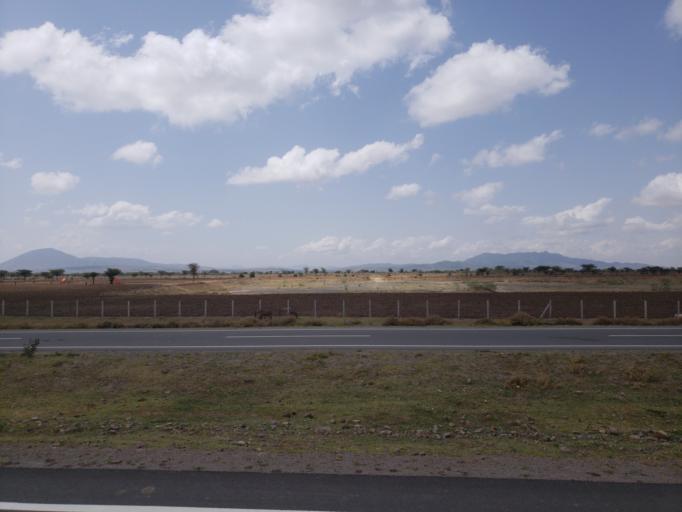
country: ET
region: Oromiya
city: Mojo
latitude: 8.2863
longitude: 38.9191
